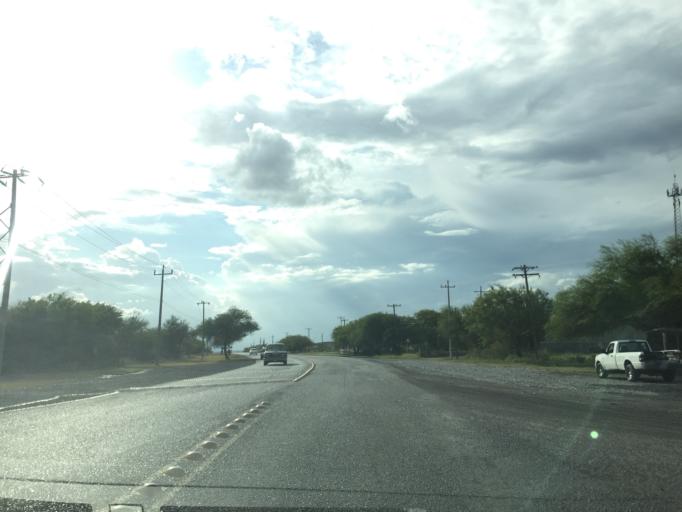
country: MX
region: Nuevo Leon
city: Marin
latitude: 25.8691
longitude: -100.0260
